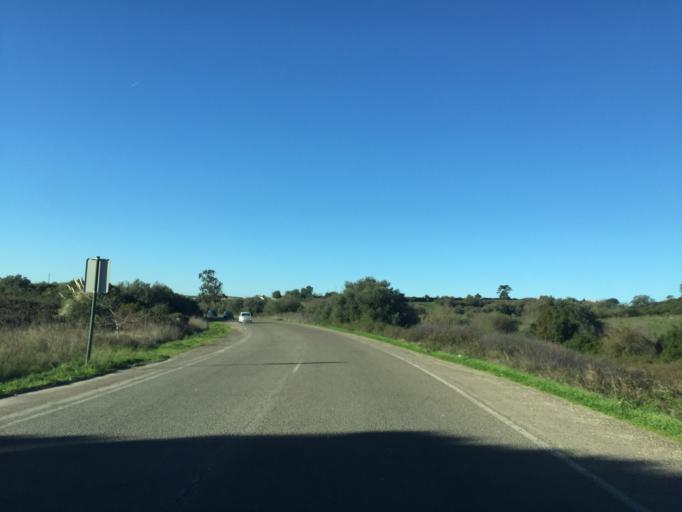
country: PT
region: Lisbon
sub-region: Sintra
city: Pero Pinheiro
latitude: 38.8640
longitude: -9.3030
